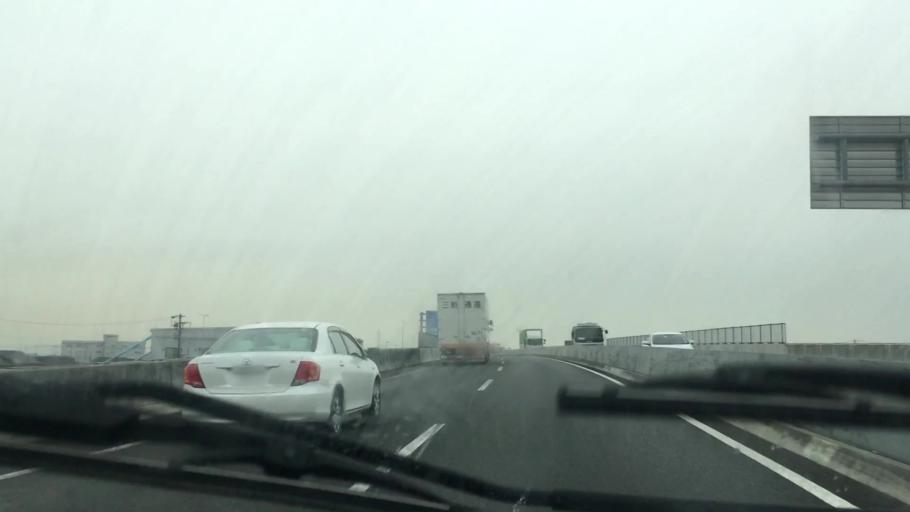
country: JP
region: Aichi
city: Anjo
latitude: 34.9331
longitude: 137.0437
